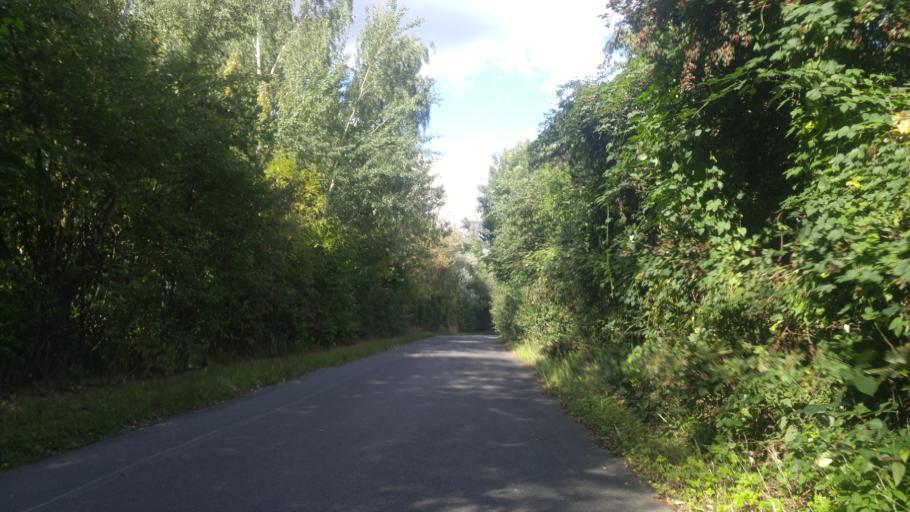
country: DE
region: North Rhine-Westphalia
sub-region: Regierungsbezirk Dusseldorf
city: Meerbusch
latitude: 51.2567
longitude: 6.6463
